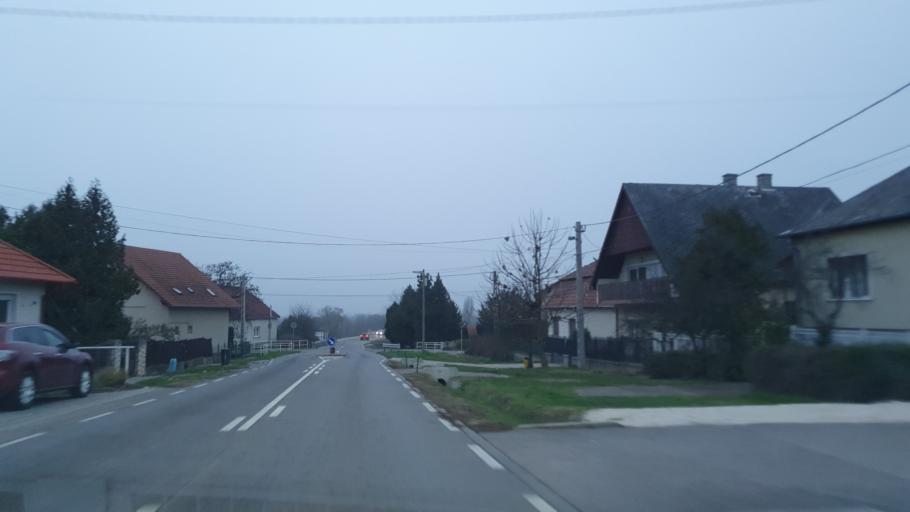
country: HU
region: Pest
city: Csomor
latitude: 47.5388
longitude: 19.2236
